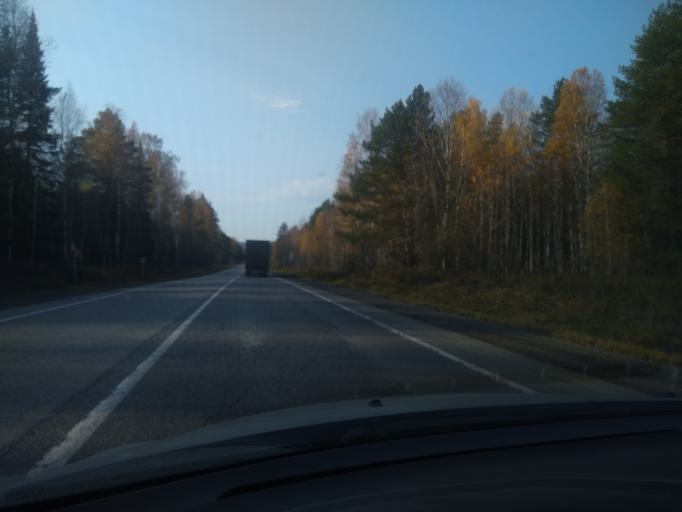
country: RU
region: Sverdlovsk
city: Atig
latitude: 56.7466
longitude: 59.4604
